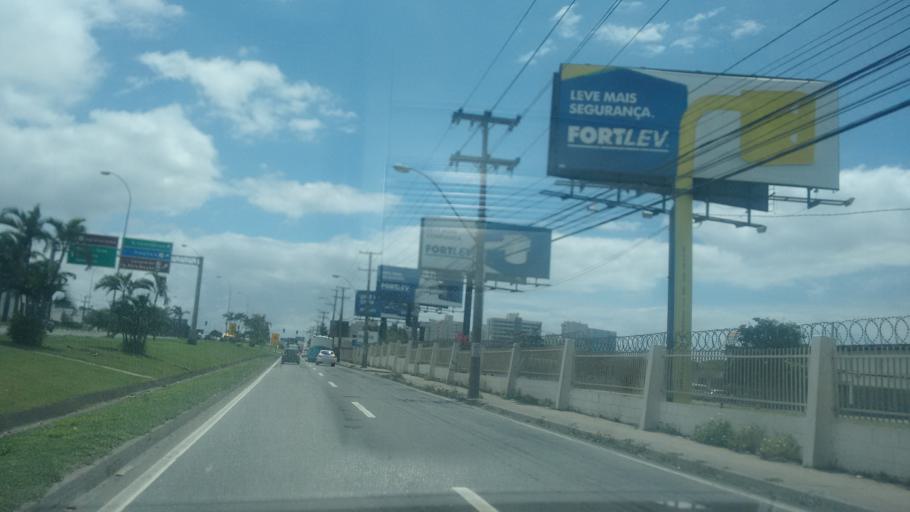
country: BR
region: Espirito Santo
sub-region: Serra
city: Serra
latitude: -20.1978
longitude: -40.2687
